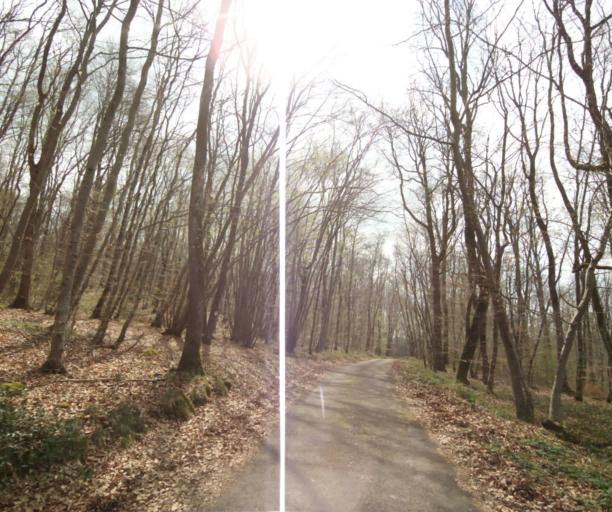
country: FR
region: Bourgogne
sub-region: Departement de Saone-et-Loire
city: Charolles
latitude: 46.3887
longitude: 4.2716
